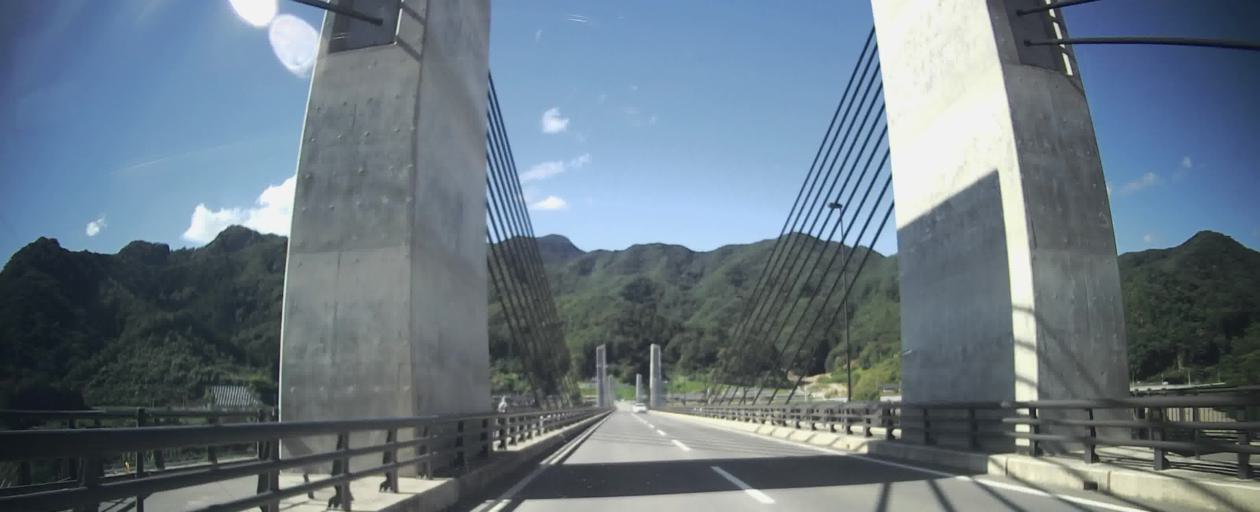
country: JP
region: Gunma
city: Nakanojomachi
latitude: 36.5520
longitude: 138.7069
